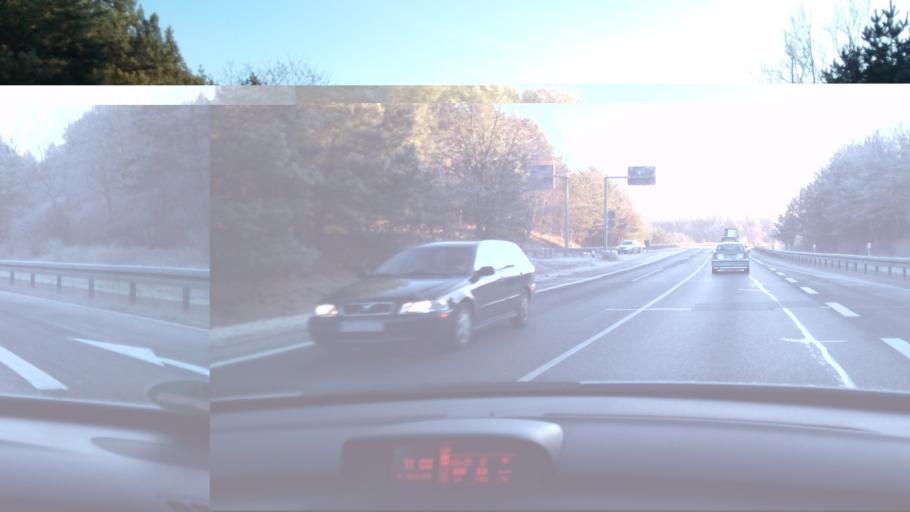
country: DE
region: Mecklenburg-Vorpommern
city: Neustrelitz
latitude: 53.3716
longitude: 13.0830
